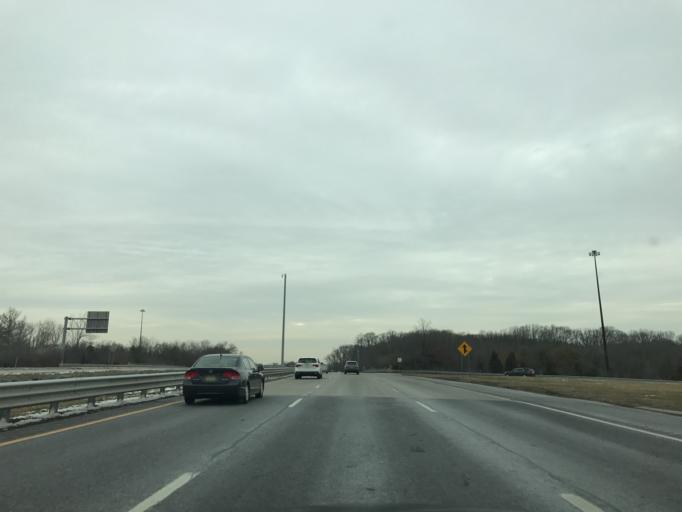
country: US
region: New Jersey
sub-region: Burlington County
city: Bordentown
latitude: 40.1339
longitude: -74.7153
